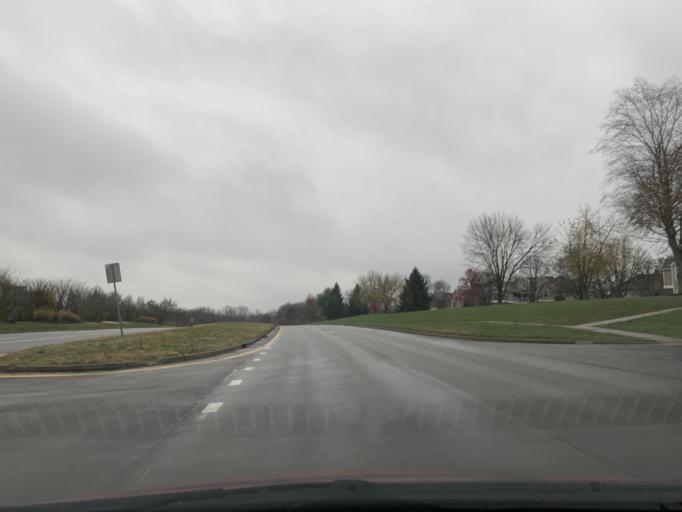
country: US
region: Kentucky
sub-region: Jefferson County
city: Hurstbourne Acres
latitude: 38.2007
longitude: -85.6027
